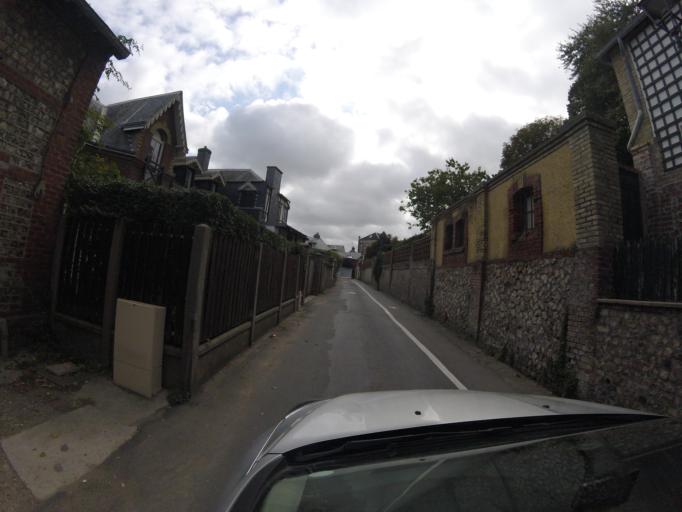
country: FR
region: Haute-Normandie
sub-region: Departement de la Seine-Maritime
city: Etretat
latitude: 49.7066
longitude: 0.2025
